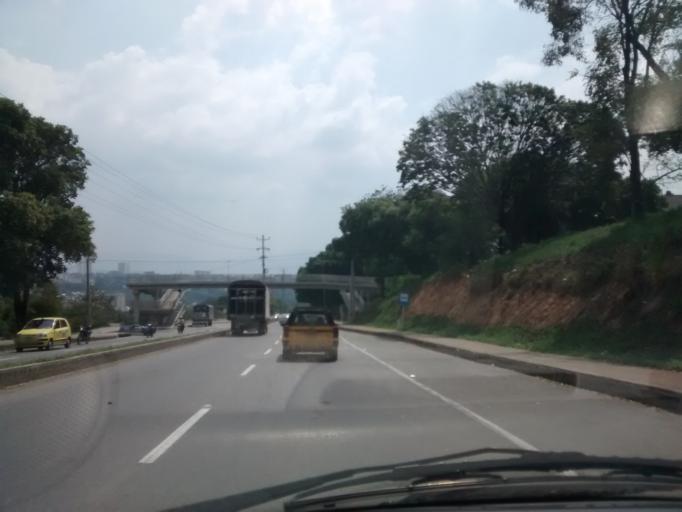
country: CO
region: Santander
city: Bucaramanga
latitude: 7.0992
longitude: -73.1137
